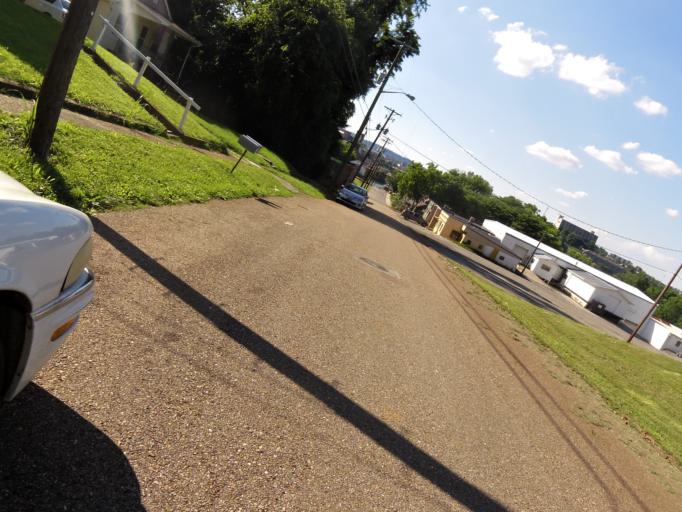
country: US
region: Tennessee
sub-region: Knox County
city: Knoxville
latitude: 35.9545
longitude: -83.9087
